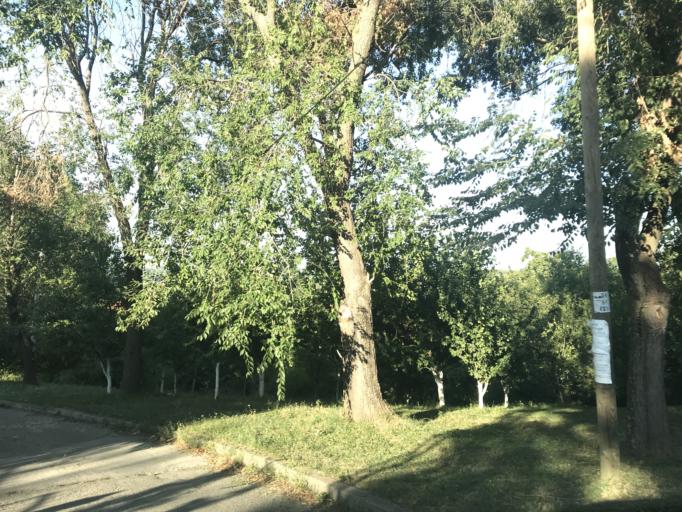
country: RS
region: Autonomna Pokrajina Vojvodina
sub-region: Juznobacki Okrug
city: Novi Sad
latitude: 45.2116
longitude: 19.8029
